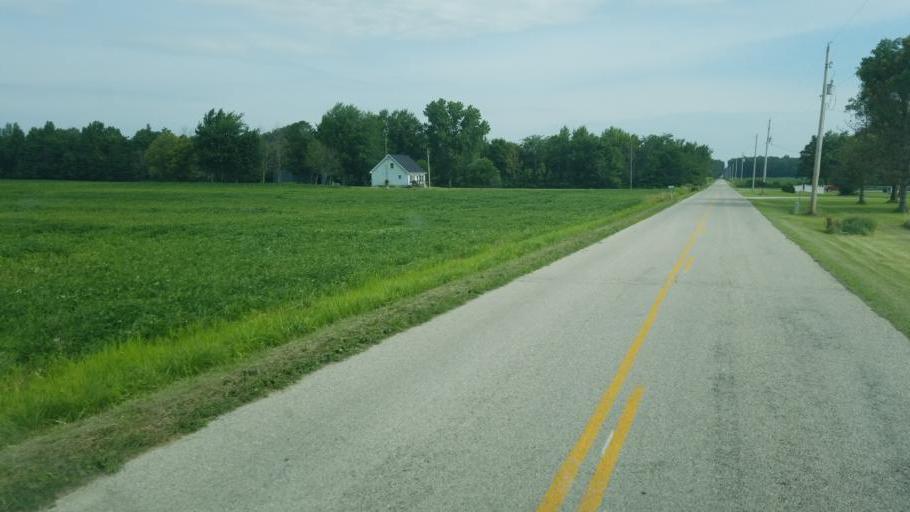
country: US
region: Ohio
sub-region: Marion County
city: Marion
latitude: 40.6275
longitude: -83.3050
